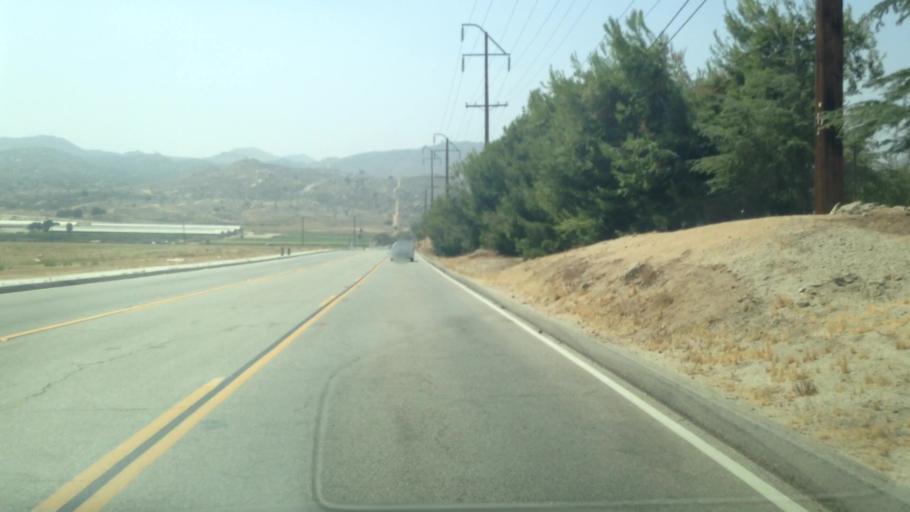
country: US
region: California
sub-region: Riverside County
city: Mead Valley
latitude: 33.8398
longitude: -117.3312
